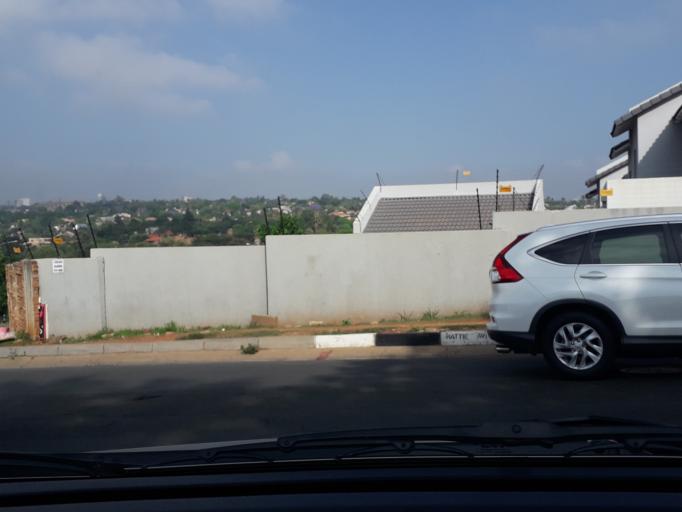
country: ZA
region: Gauteng
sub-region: City of Johannesburg Metropolitan Municipality
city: Johannesburg
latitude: -26.0924
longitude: 28.0297
